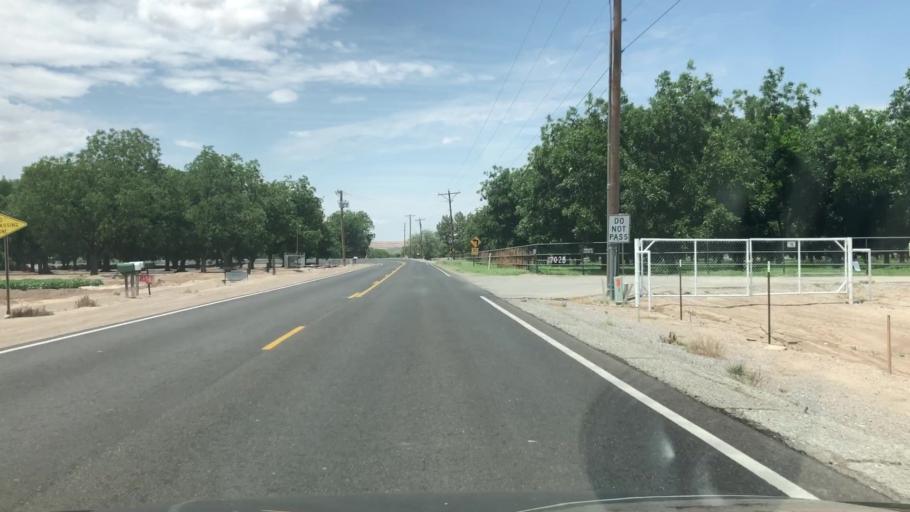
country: US
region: New Mexico
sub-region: Dona Ana County
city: La Union
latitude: 31.9208
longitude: -106.6394
